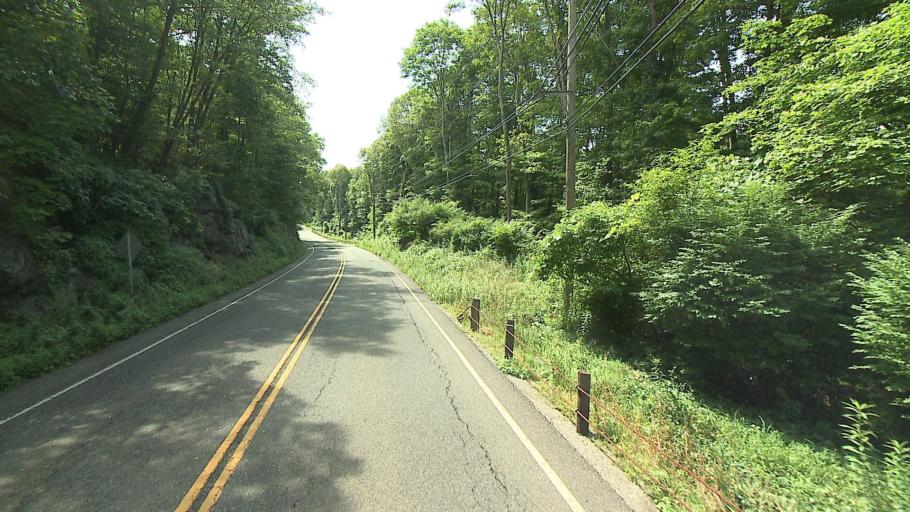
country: US
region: Connecticut
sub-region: Fairfield County
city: Sherman
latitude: 41.5493
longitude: -73.4819
